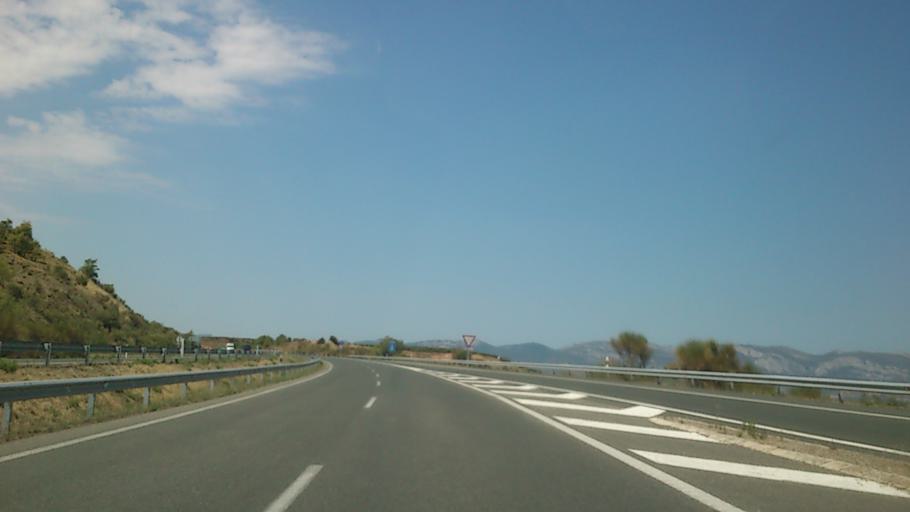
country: ES
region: La Rioja
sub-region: Provincia de La Rioja
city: Cenicero
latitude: 42.4707
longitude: -2.6466
